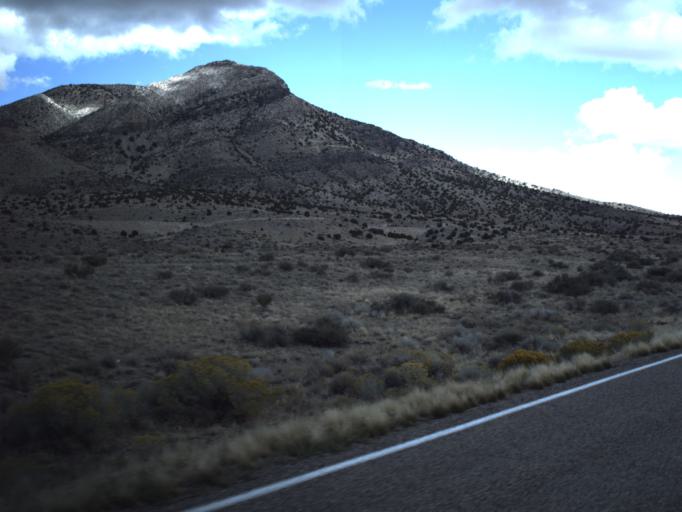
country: US
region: Utah
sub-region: Beaver County
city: Milford
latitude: 38.4361
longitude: -113.3027
